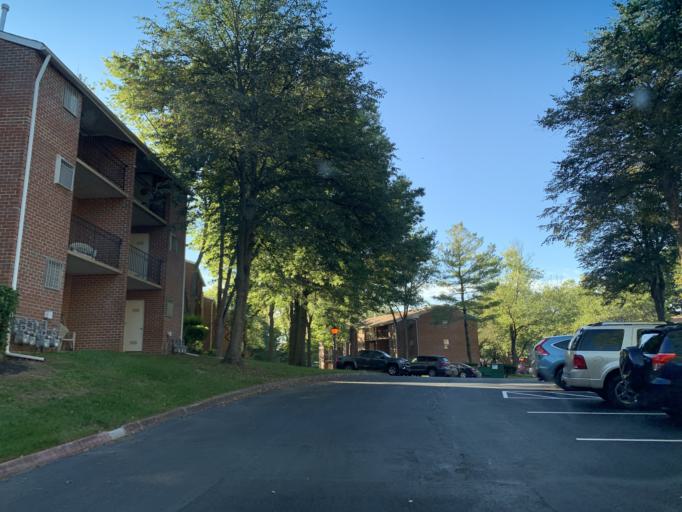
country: US
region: Maryland
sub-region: Harford County
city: Bel Air North
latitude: 39.5599
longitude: -76.3749
